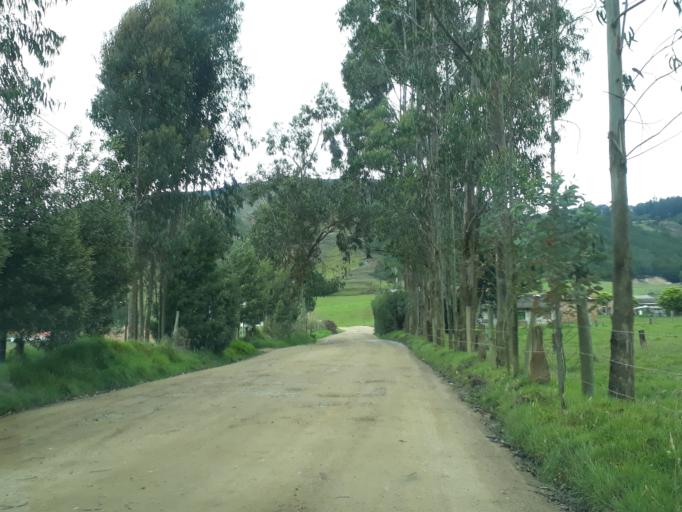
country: CO
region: Cundinamarca
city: Cucunuba
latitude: 5.2047
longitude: -73.7665
